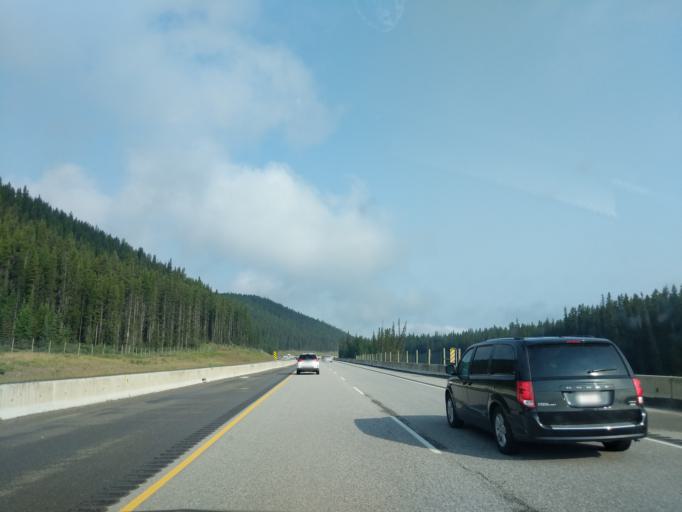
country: CA
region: Alberta
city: Lake Louise
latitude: 51.3244
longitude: -116.0444
